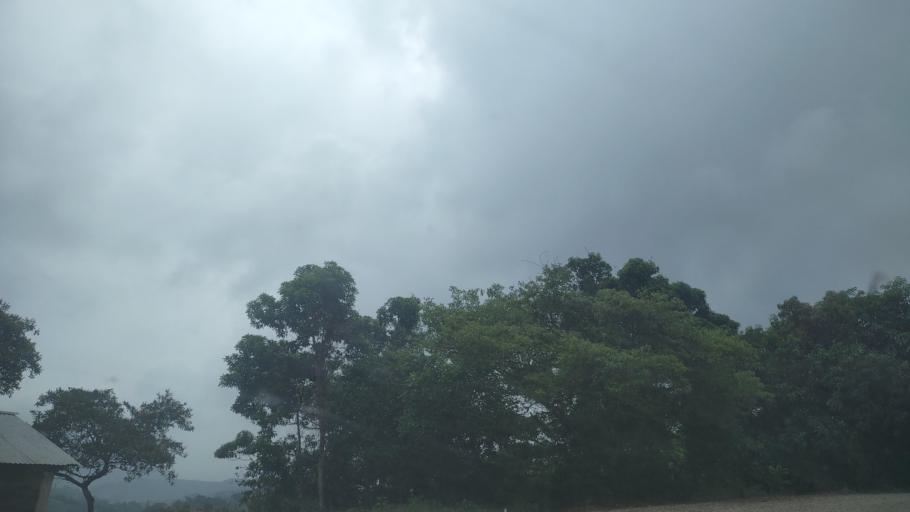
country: MX
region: Tabasco
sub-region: Huimanguillo
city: Francisco Rueda
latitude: 17.4384
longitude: -94.0234
